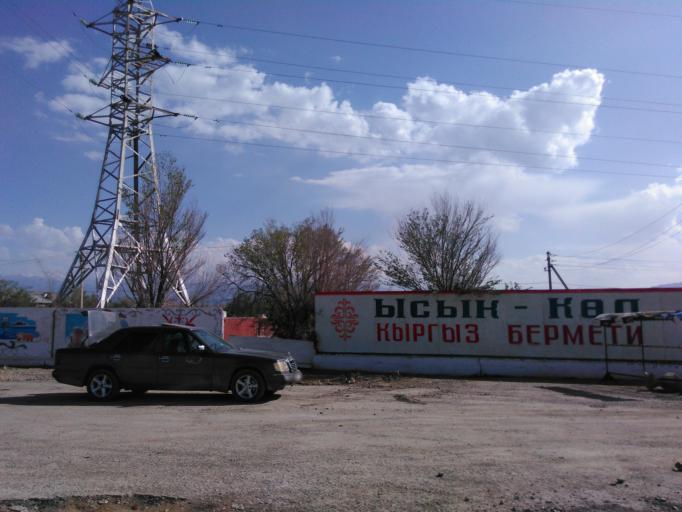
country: KG
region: Ysyk-Koel
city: Balykchy
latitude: 42.4535
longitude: 76.1605
